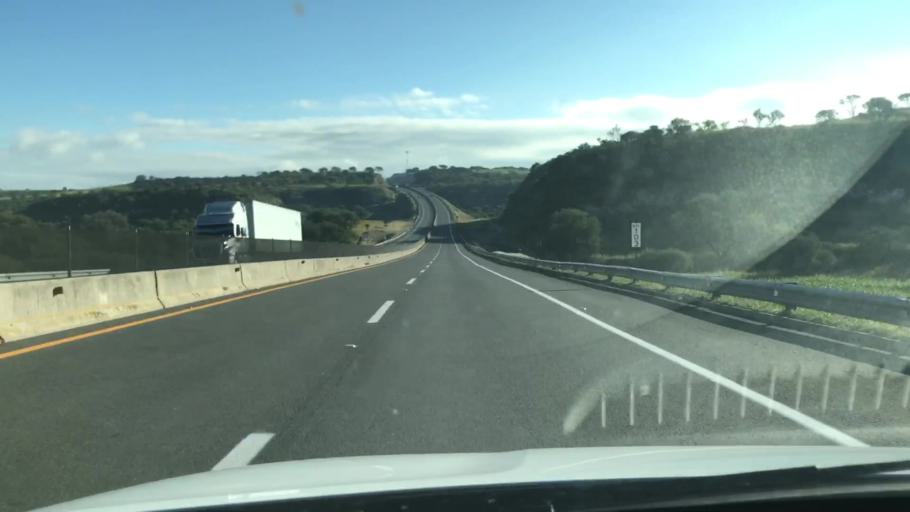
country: MX
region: Jalisco
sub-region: San Juan de los Lagos
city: Mezquitic de la Magdalena
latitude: 21.1895
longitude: -102.3524
